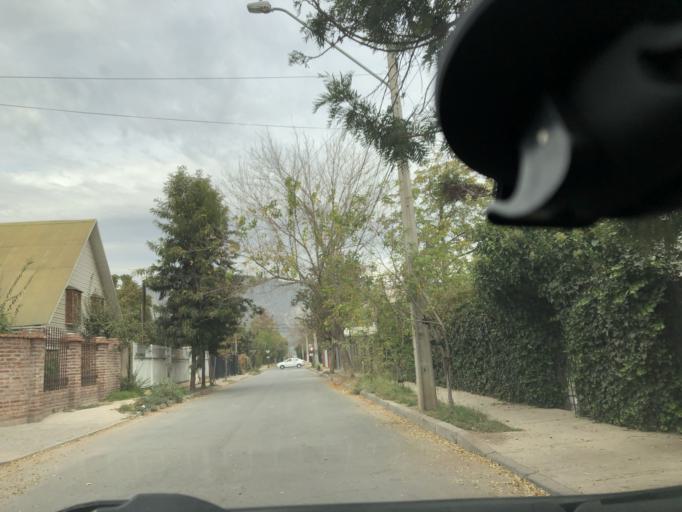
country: CL
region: Santiago Metropolitan
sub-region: Provincia de Cordillera
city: Puente Alto
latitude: -33.6073
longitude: -70.5262
